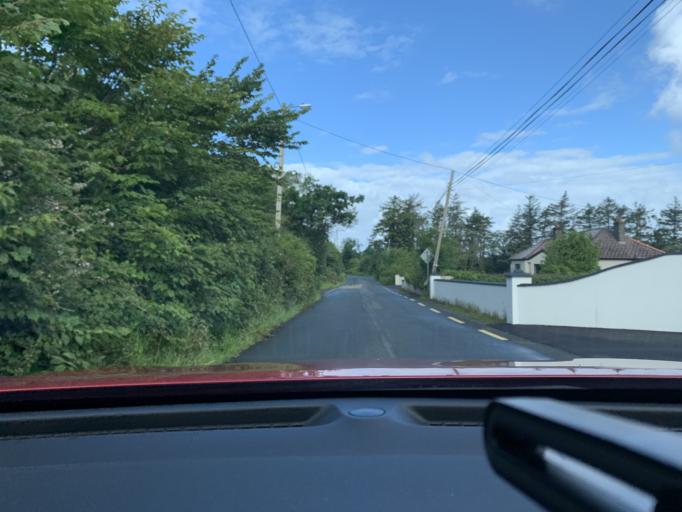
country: IE
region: Connaught
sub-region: Sligo
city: Sligo
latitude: 54.3924
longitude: -8.5286
